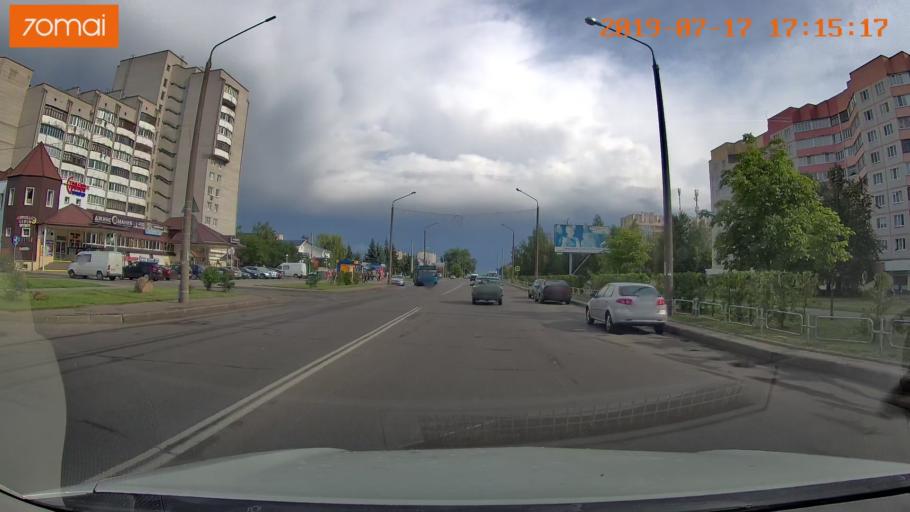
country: BY
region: Mogilev
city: Babruysk
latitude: 53.1703
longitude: 29.1913
